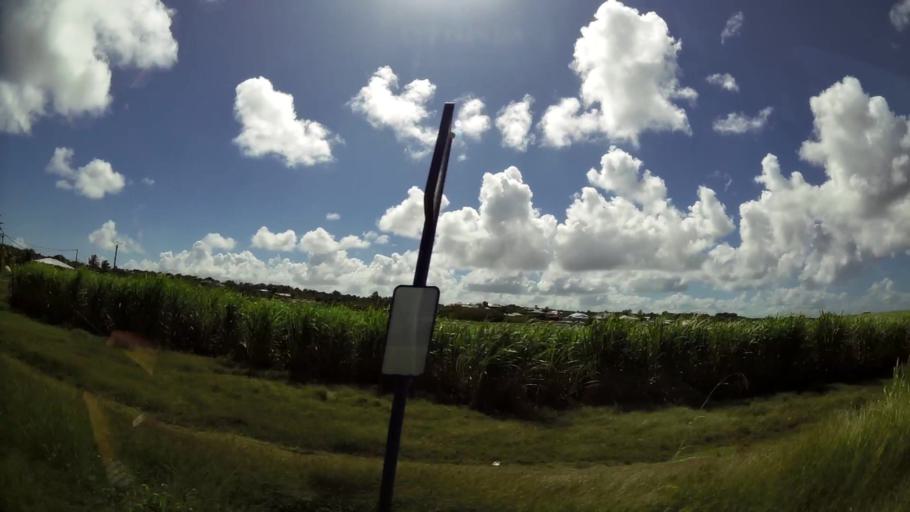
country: GP
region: Guadeloupe
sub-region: Guadeloupe
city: Anse-Bertrand
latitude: 16.4616
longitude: -61.4829
